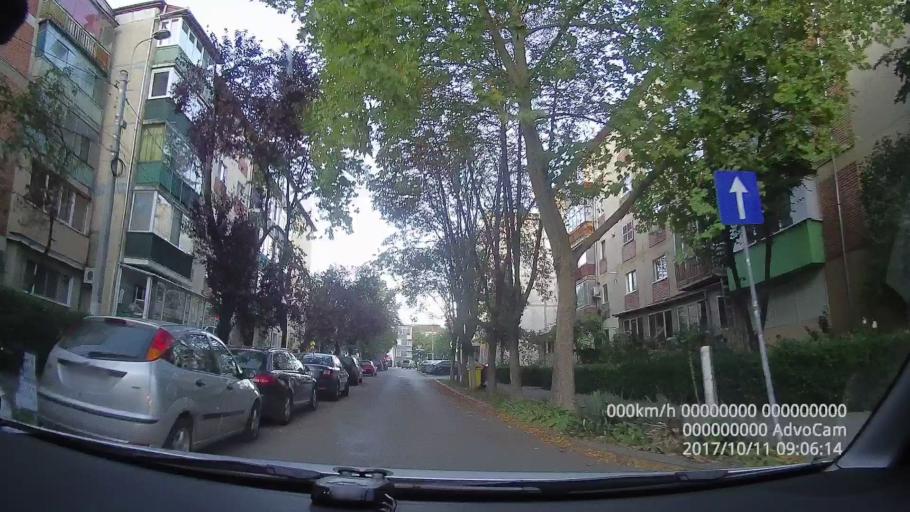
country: RO
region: Timis
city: Timisoara
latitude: 45.7768
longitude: 21.2223
